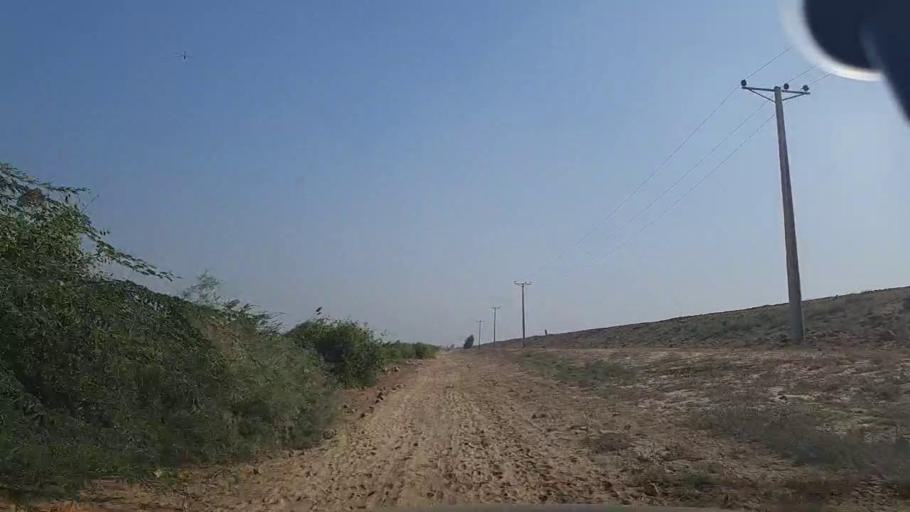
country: PK
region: Sindh
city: Chuhar Jamali
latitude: 24.4612
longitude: 67.9055
